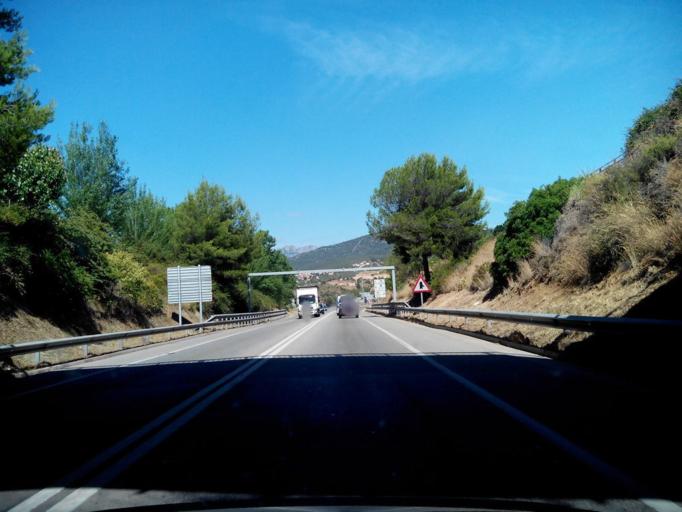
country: ES
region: Catalonia
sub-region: Provincia de Barcelona
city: Viladecavalls
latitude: 41.5580
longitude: 1.9829
